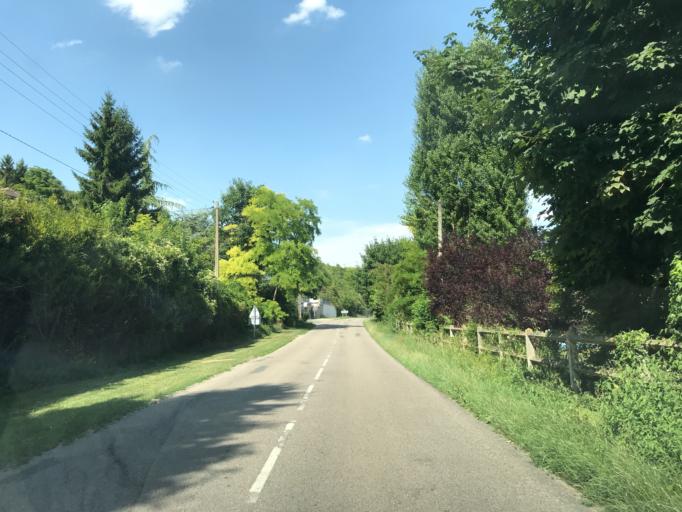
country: FR
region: Ile-de-France
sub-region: Departement des Yvelines
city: Bonnieres-sur-Seine
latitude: 49.0463
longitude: 1.5822
